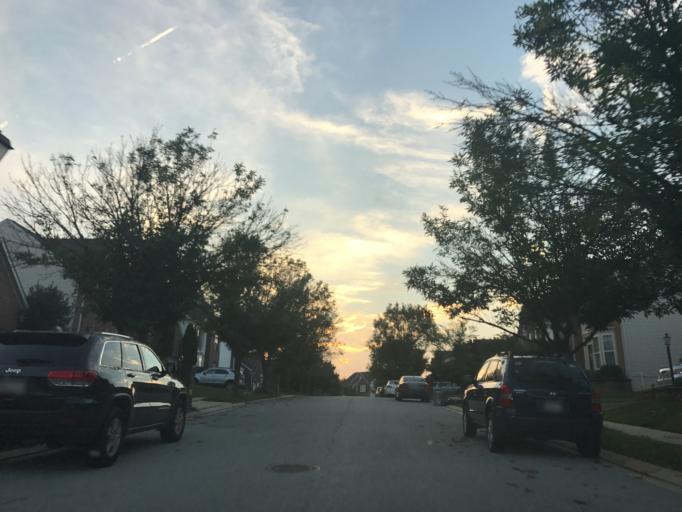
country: US
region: Maryland
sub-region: Baltimore County
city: Perry Hall
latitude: 39.4107
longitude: -76.4370
